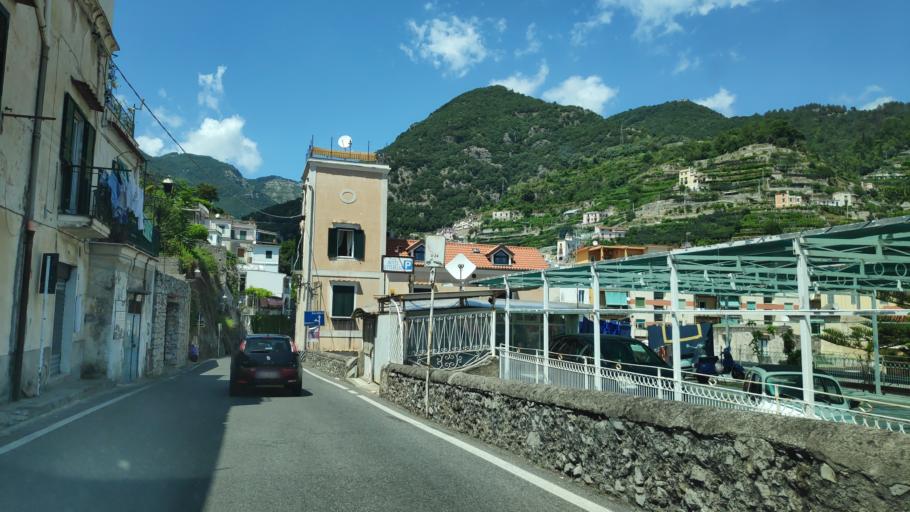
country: IT
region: Campania
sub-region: Provincia di Salerno
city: Minori
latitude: 40.6500
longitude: 14.6256
